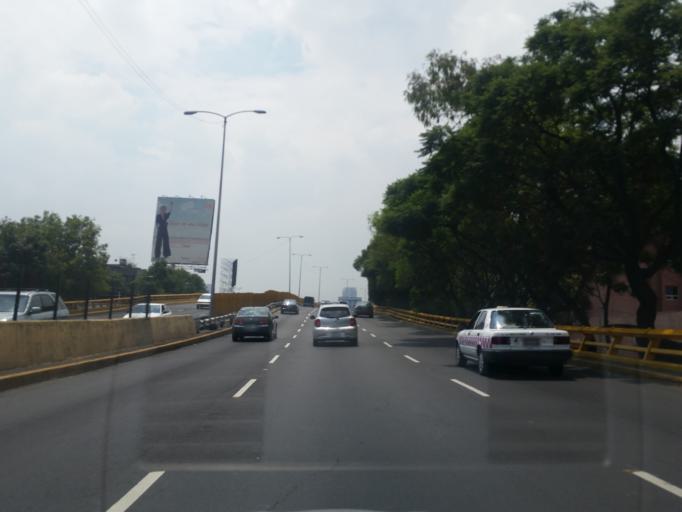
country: MX
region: Mexico City
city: Cuauhtemoc
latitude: 19.4517
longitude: -99.1643
